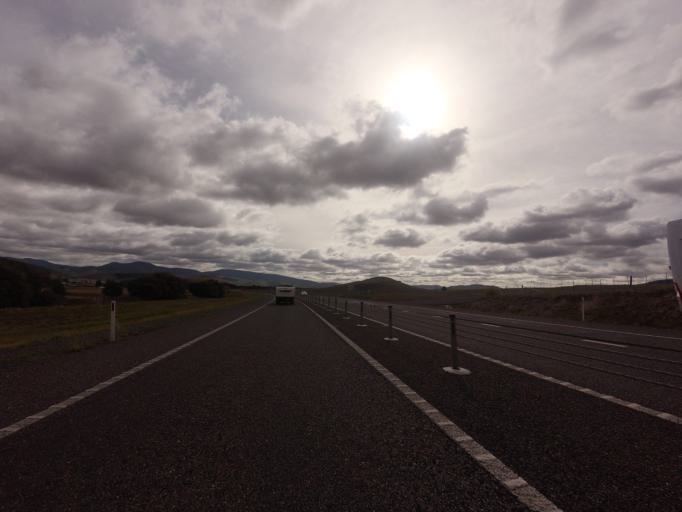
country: AU
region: Tasmania
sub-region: Brighton
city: Bridgewater
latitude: -42.5269
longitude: 147.2013
